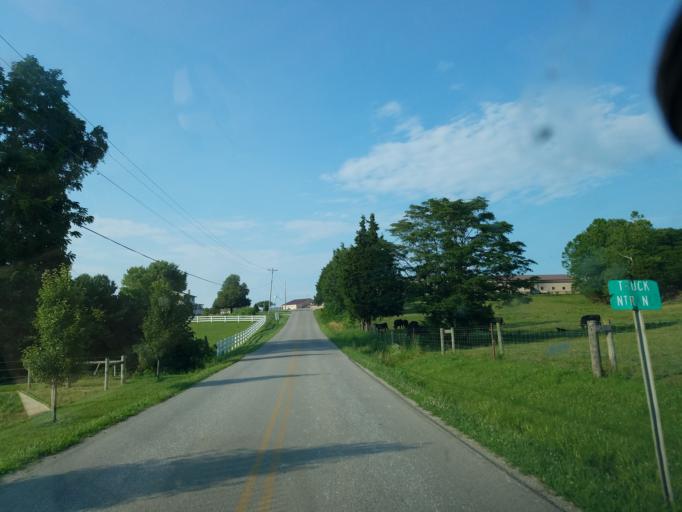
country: US
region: Ohio
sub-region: Adams County
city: West Union
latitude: 38.8956
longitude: -83.5206
